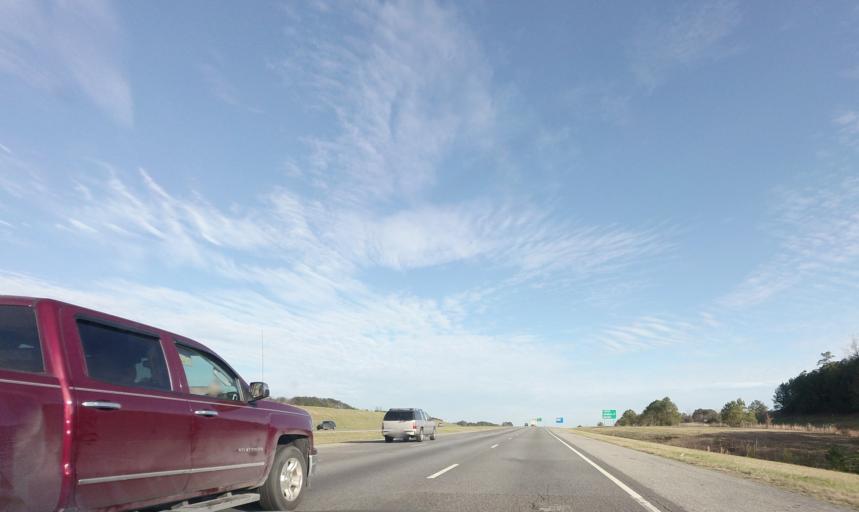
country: US
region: Alabama
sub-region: Walker County
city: Jasper
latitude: 33.8569
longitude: -87.3623
